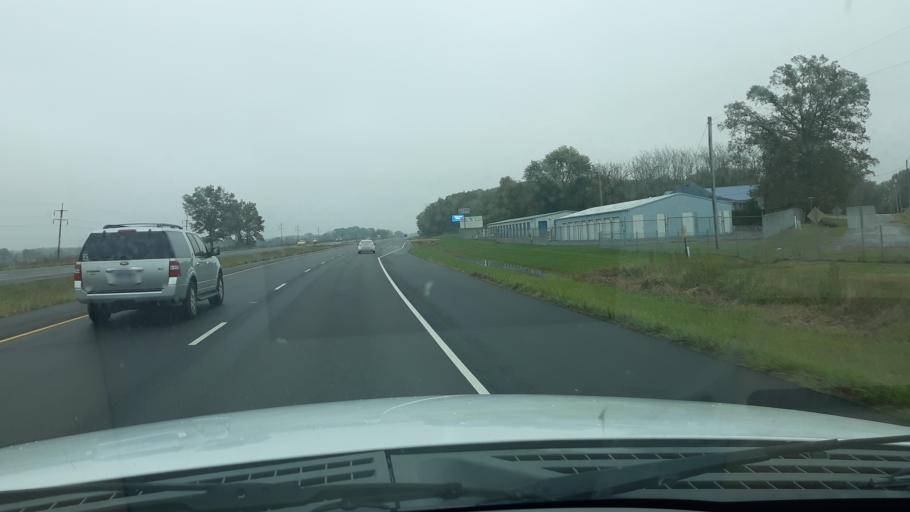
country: US
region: Illinois
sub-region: Saline County
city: Eldorado
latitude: 37.7899
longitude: -88.4811
